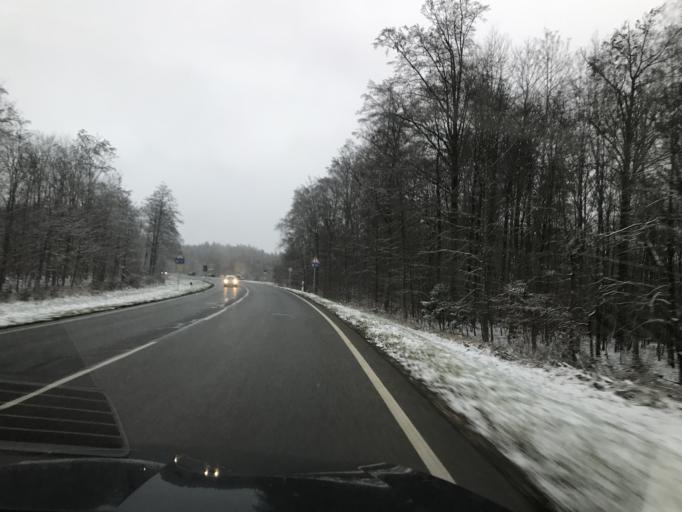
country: DE
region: Baden-Wuerttemberg
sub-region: Regierungsbezirk Stuttgart
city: Altbach
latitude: 48.7355
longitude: 9.4014
